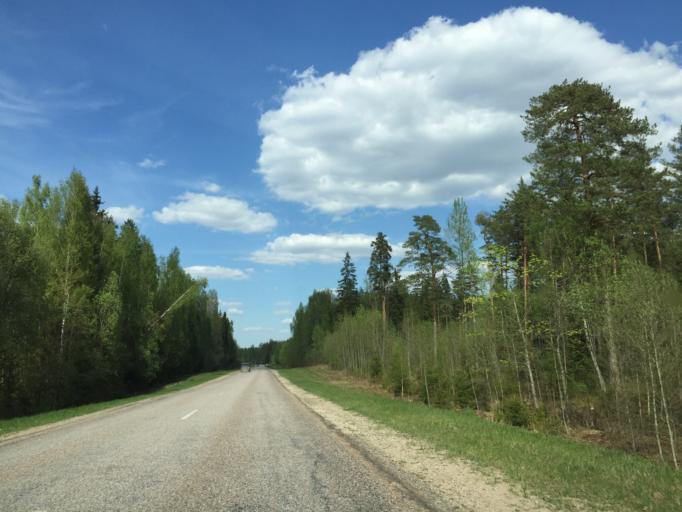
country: LV
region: Limbazu Rajons
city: Limbazi
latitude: 57.4172
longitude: 24.7001
